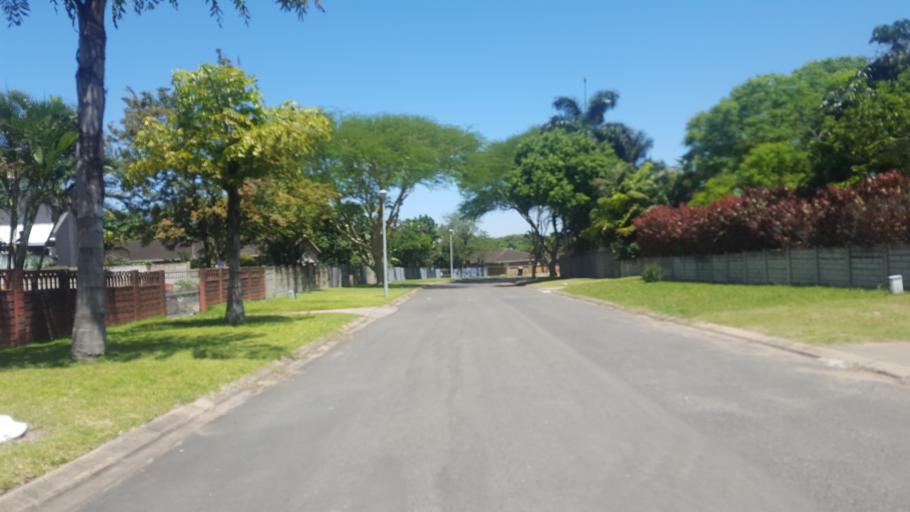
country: ZA
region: KwaZulu-Natal
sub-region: uThungulu District Municipality
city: Richards Bay
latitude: -28.7653
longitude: 32.0642
